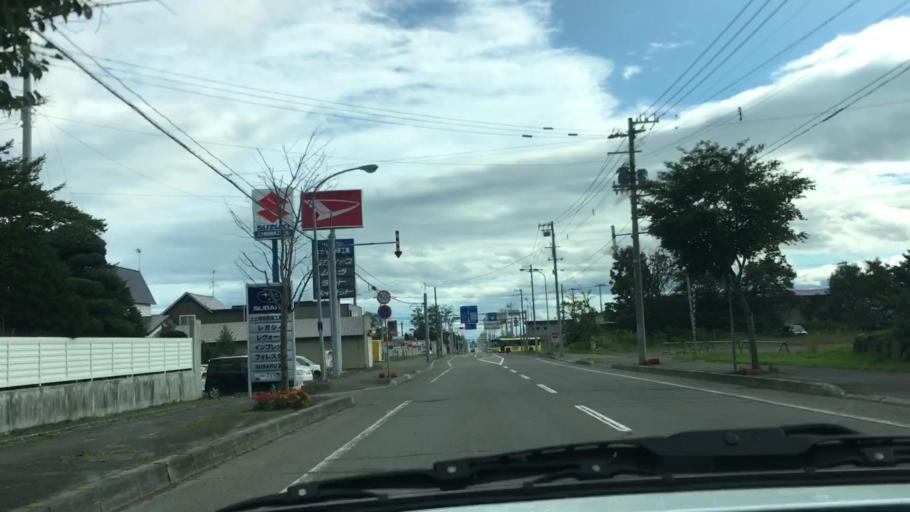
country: JP
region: Hokkaido
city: Otofuke
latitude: 43.2362
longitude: 143.2958
